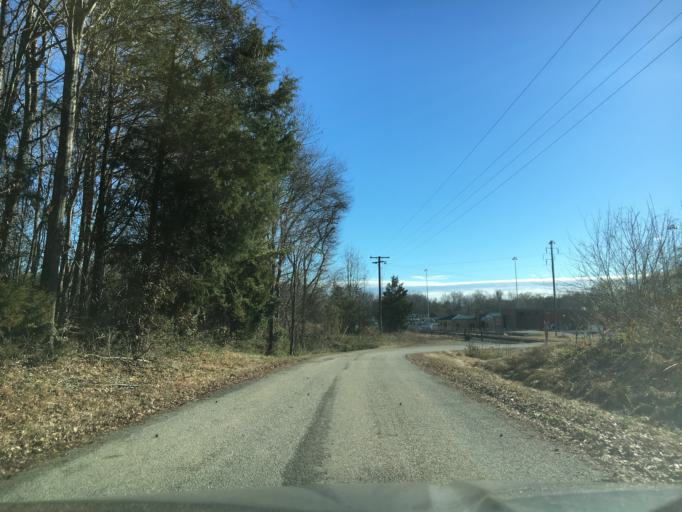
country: US
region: Virginia
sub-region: Halifax County
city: South Boston
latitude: 36.6963
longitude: -78.8832
